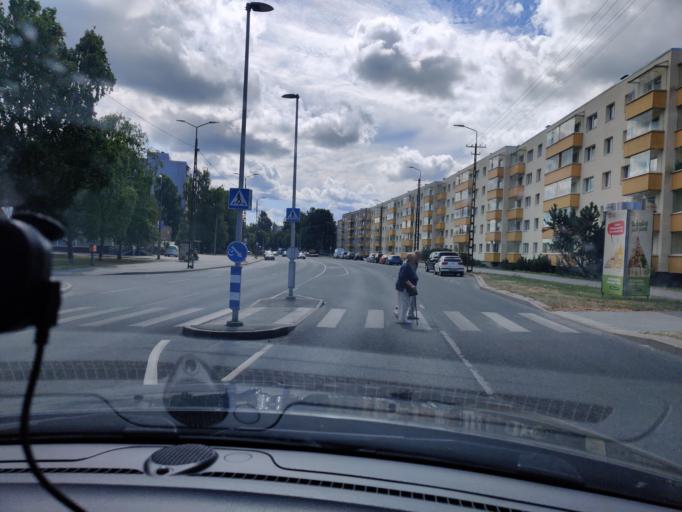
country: EE
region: Harju
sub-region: Saue vald
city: Laagri
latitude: 59.4163
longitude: 24.6397
